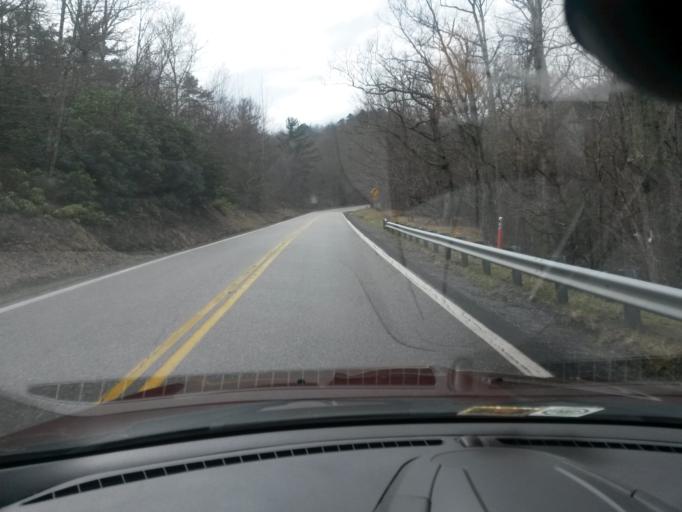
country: US
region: Virginia
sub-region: Bath County
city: Warm Springs
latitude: 38.0402
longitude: -79.7624
